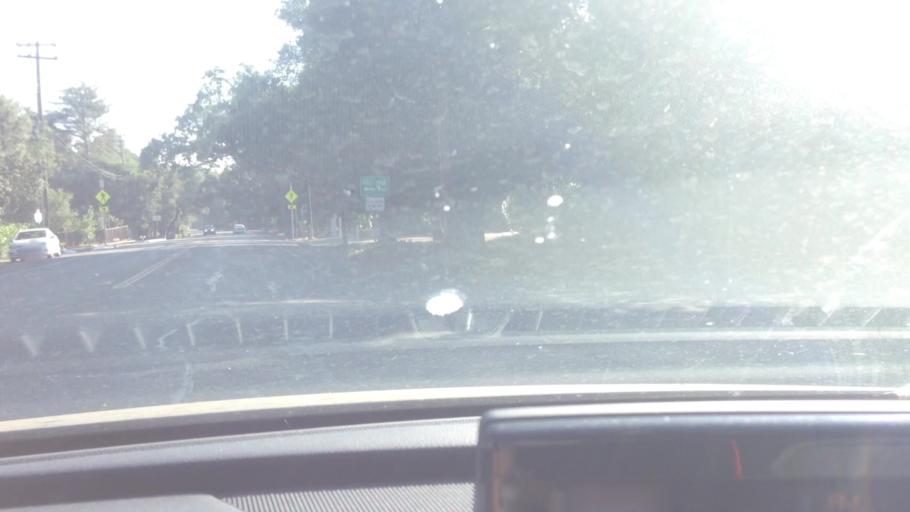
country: US
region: California
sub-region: Santa Clara County
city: Saratoga
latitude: 37.2648
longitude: -122.0225
